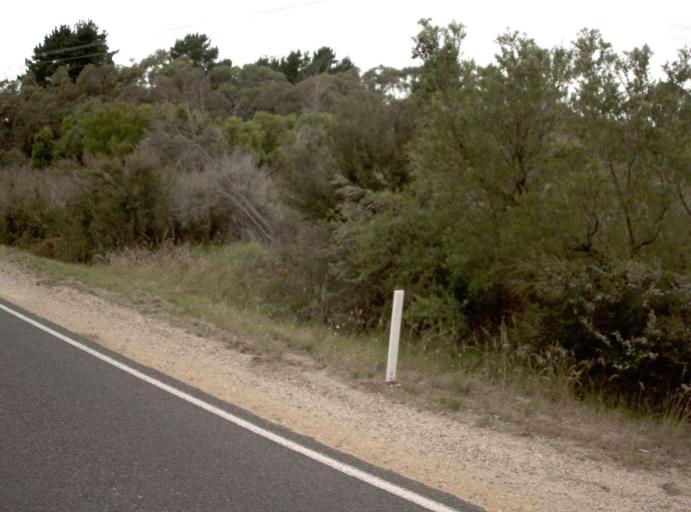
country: AU
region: Victoria
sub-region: Wellington
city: Sale
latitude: -38.1772
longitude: 147.1567
